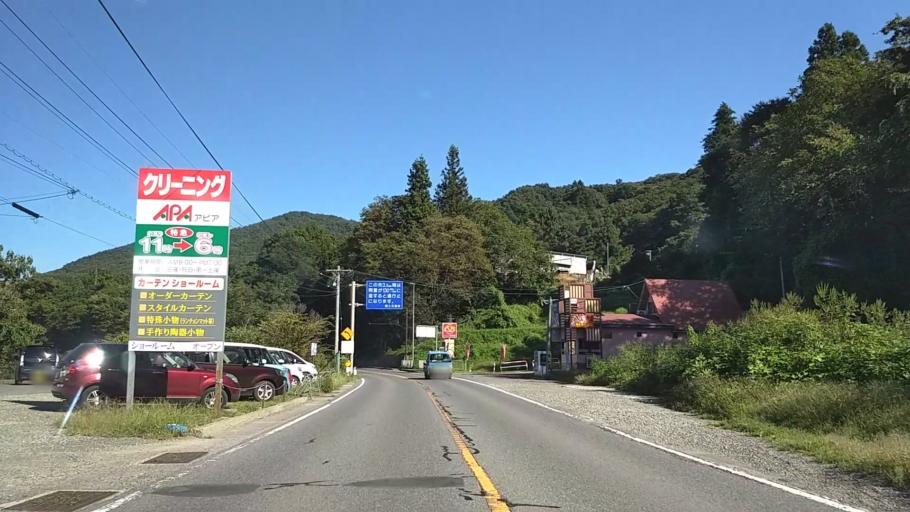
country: JP
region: Nagano
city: Nagano-shi
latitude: 36.6164
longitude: 138.0984
